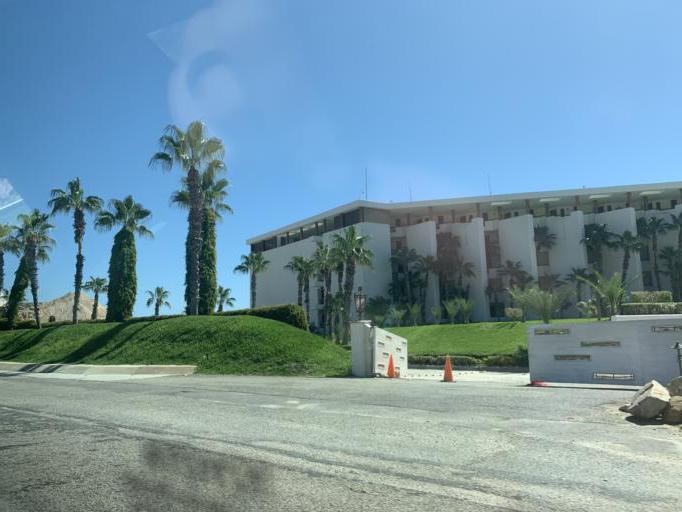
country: MX
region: Baja California Sur
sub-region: Los Cabos
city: San Jose del Cabo
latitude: 22.9869
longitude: -109.7579
